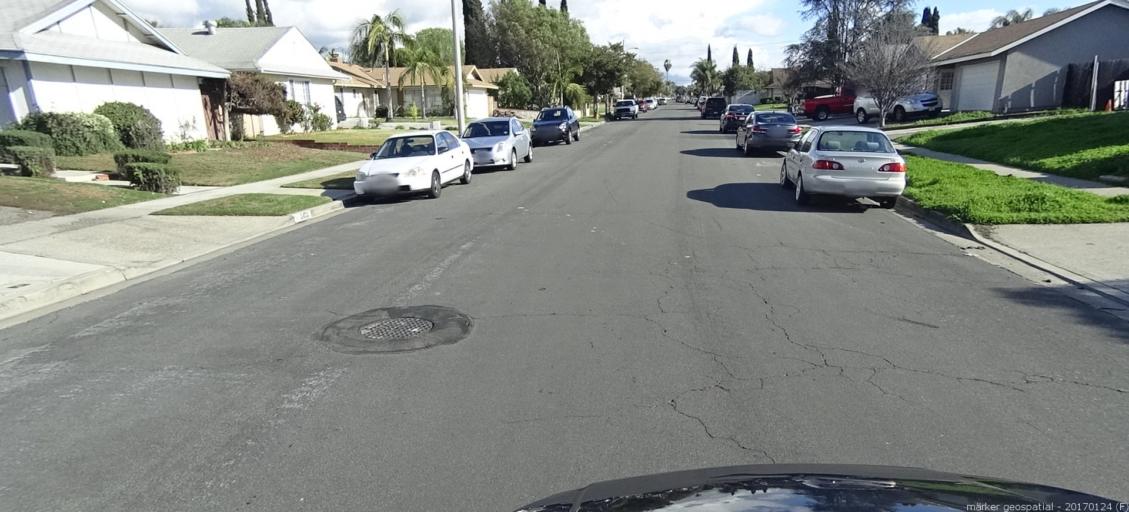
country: US
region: California
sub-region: Orange County
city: Laguna Hills
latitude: 33.6146
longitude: -117.7023
